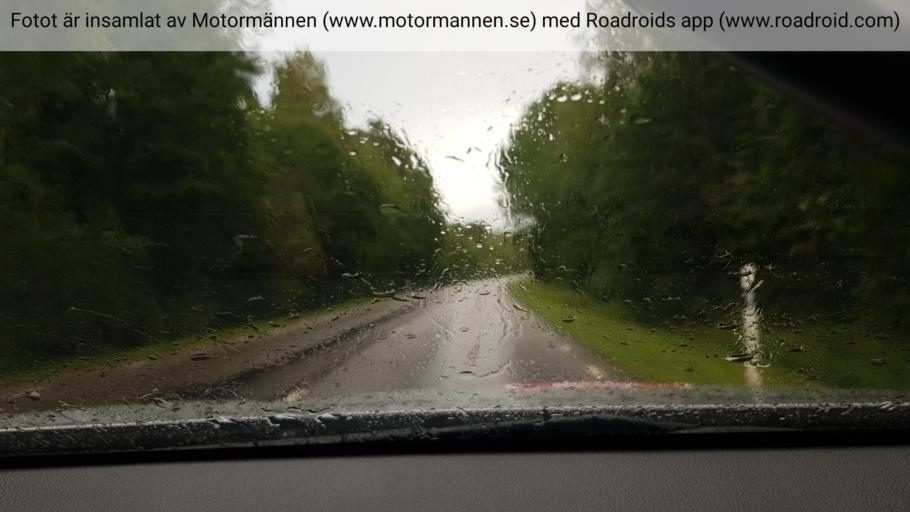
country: SE
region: Uppsala
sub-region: Tierps Kommun
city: Karlholmsbruk
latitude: 60.5135
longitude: 17.6479
